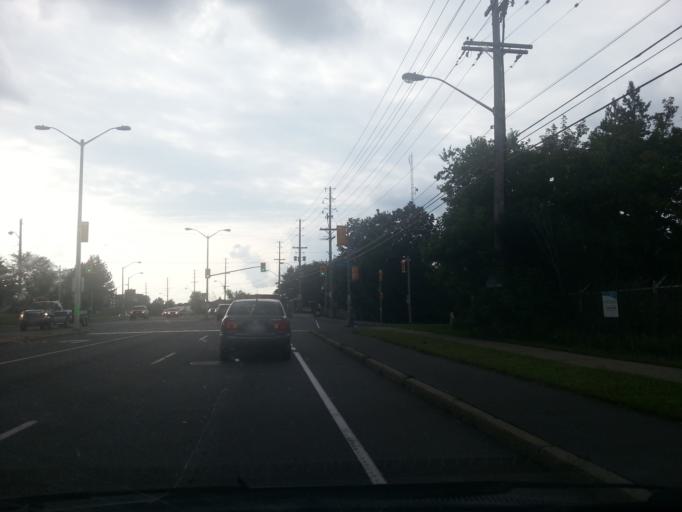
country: CA
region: Ontario
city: Ottawa
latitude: 45.4473
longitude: -75.6246
